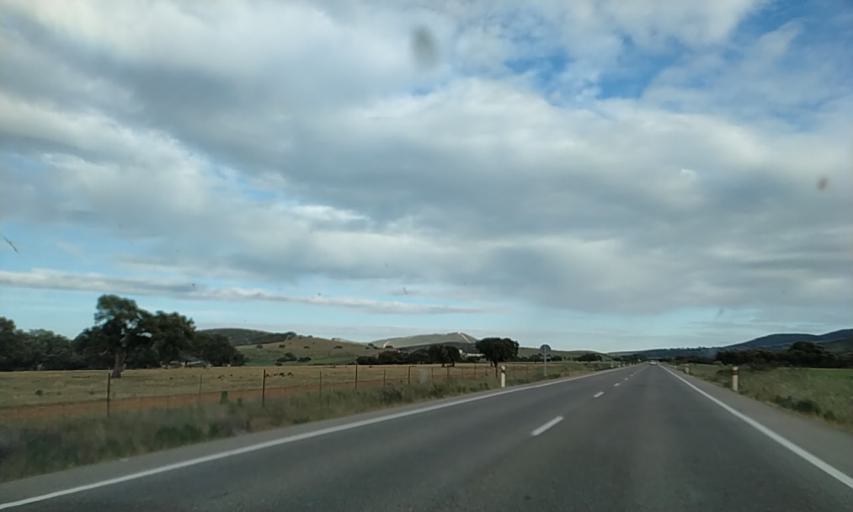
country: ES
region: Extremadura
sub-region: Provincia de Caceres
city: Pedroso de Acim
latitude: 39.8588
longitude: -6.4268
